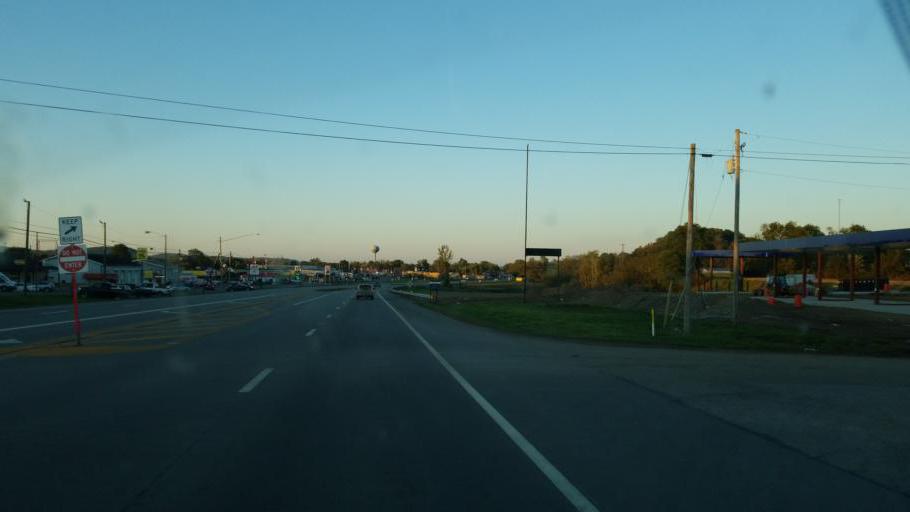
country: US
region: Ohio
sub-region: Pike County
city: Piketon
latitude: 39.0581
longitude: -83.0188
